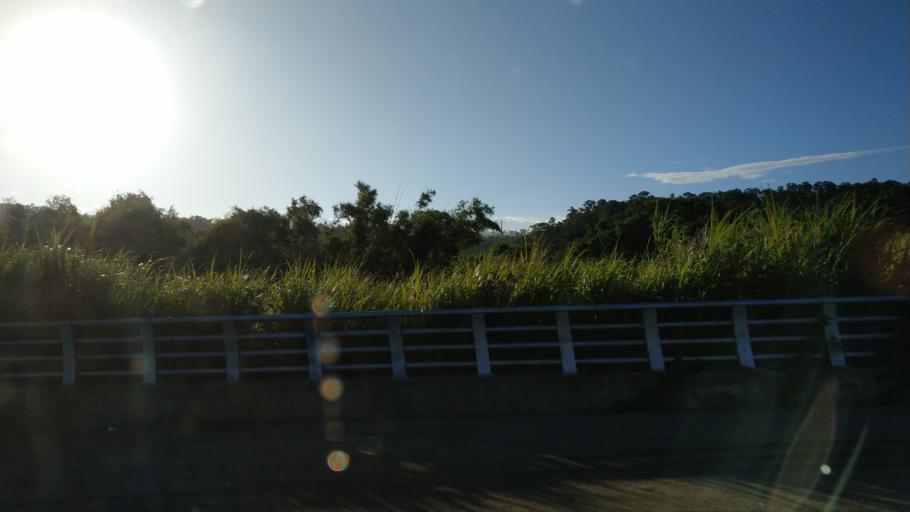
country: TW
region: Taiwan
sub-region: Miaoli
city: Miaoli
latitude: 24.5416
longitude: 120.7974
